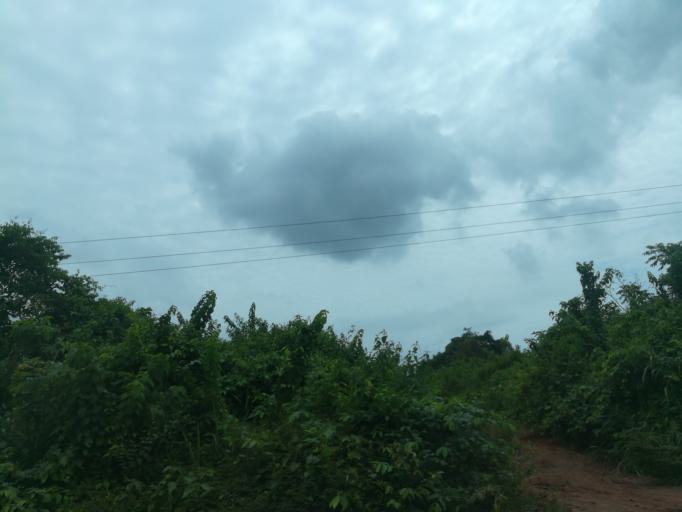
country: NG
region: Ogun
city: Odogbolu
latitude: 6.6681
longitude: 3.7102
